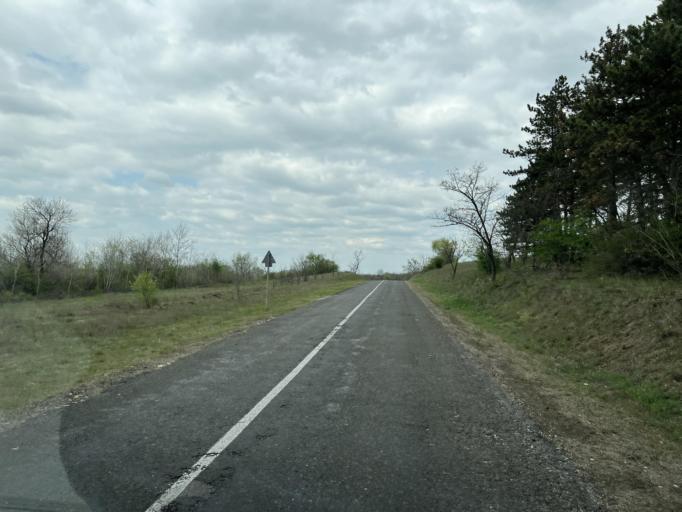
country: HU
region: Pest
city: Dabas
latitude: 47.1230
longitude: 19.3519
